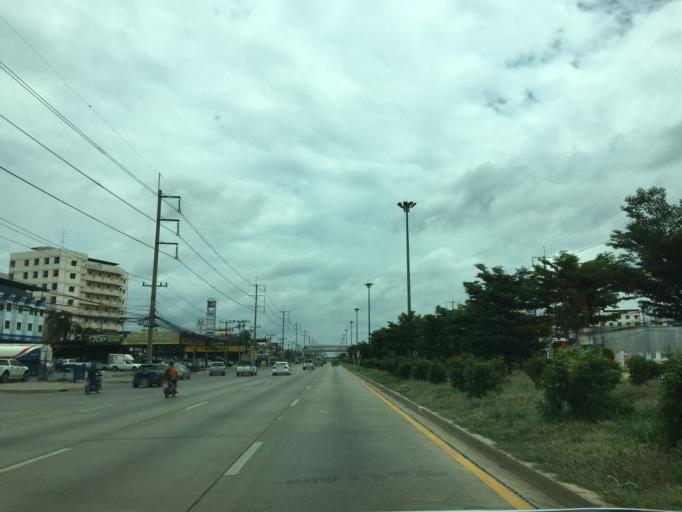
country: TH
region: Phra Nakhon Si Ayutthaya
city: Uthai
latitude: 14.3209
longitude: 100.6328
